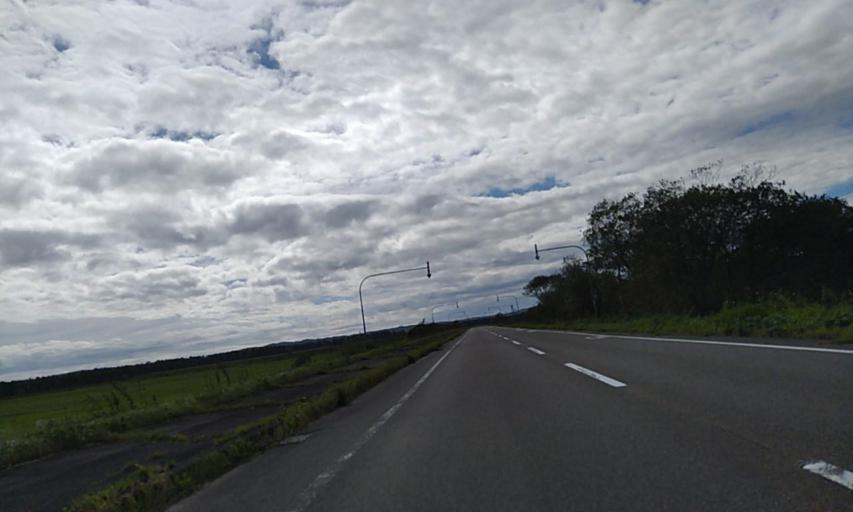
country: JP
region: Hokkaido
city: Obihiro
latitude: 42.7199
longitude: 143.6511
